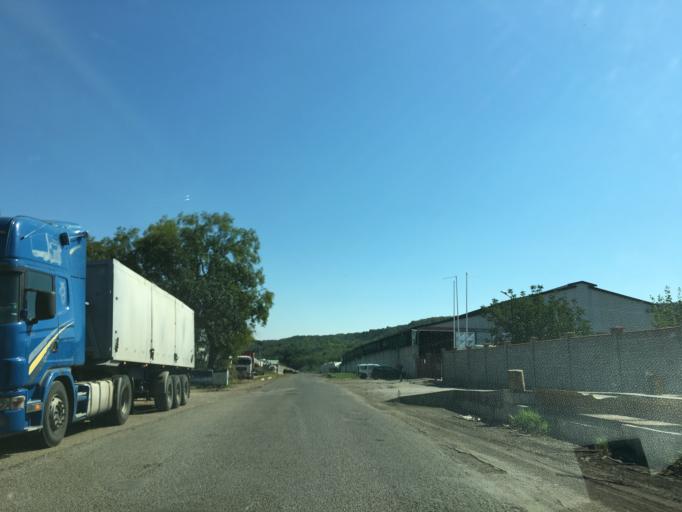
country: RO
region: Dolj
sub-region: Comuna Desa
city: Desa
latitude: 43.7656
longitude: 23.0155
